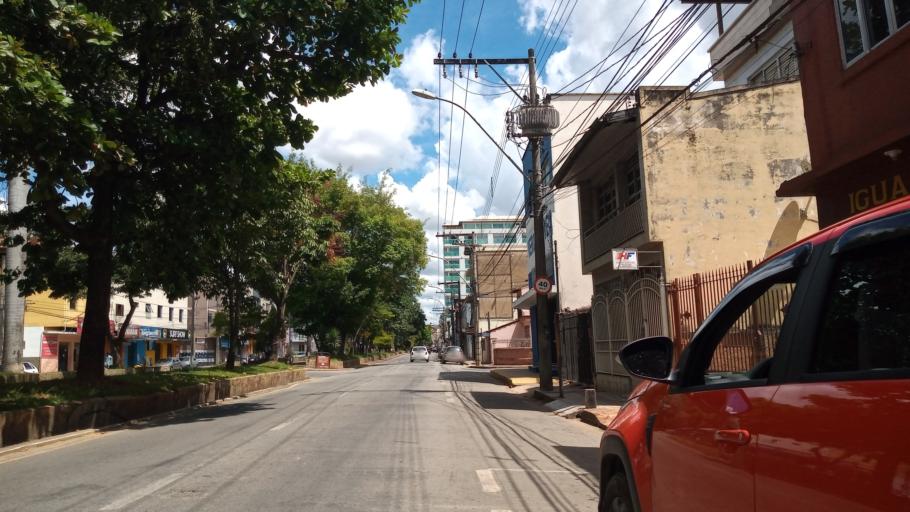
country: BR
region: Minas Gerais
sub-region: Sao Joao Del Rei
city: Sao Joao del Rei
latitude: -21.1219
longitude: -44.2469
